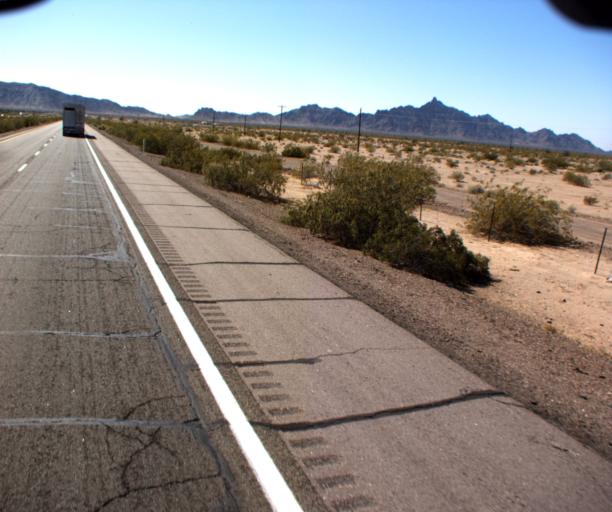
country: US
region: Arizona
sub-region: Yuma County
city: Wellton
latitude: 32.7422
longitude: -113.6848
